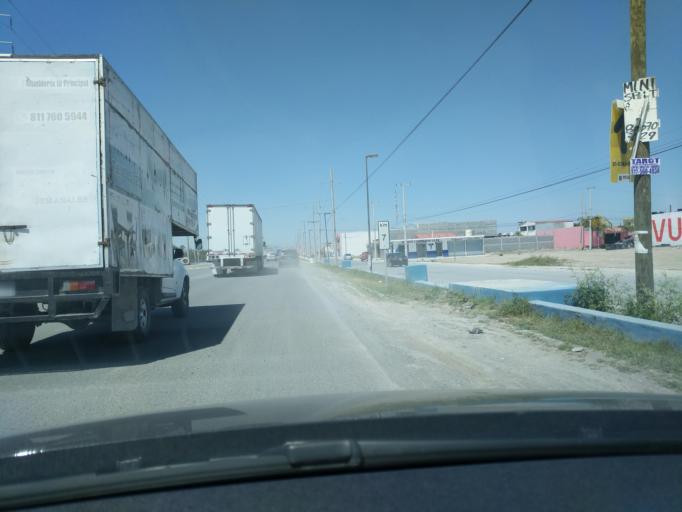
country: MX
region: Nuevo Leon
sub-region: Salinas Victoria
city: Emiliano Zapata
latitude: 25.9114
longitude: -100.2670
